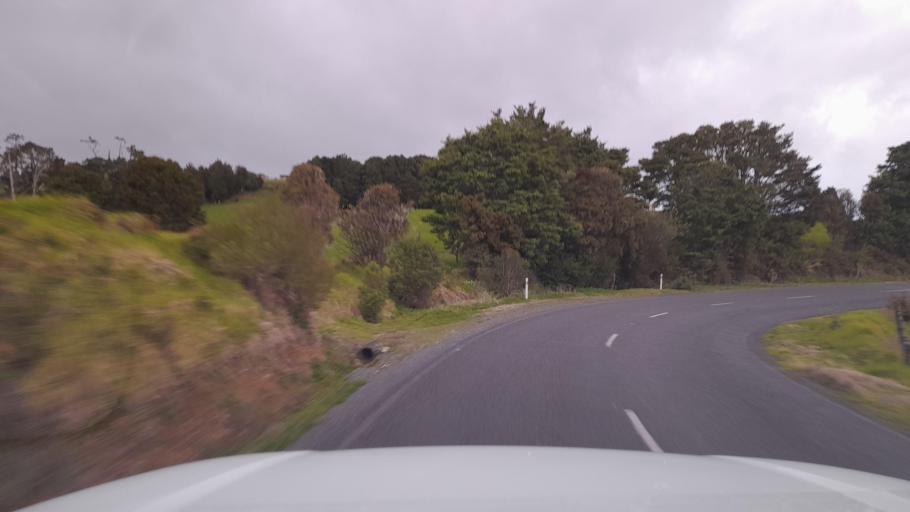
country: NZ
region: Northland
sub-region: Whangarei
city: Maungatapere
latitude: -35.6440
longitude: 174.2190
